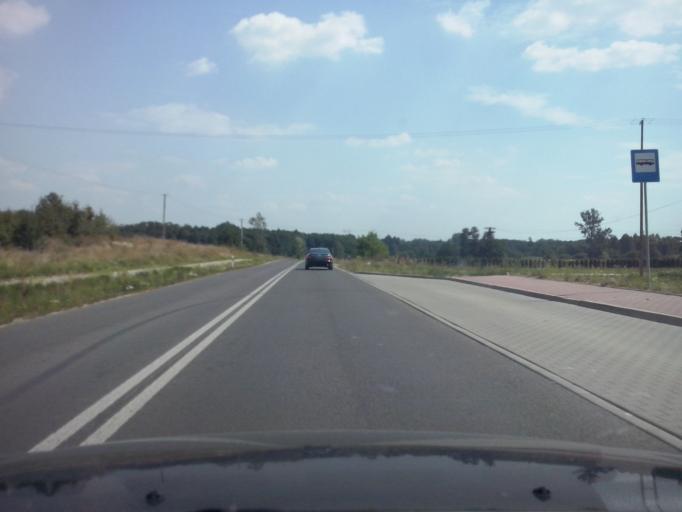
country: PL
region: Swietokrzyskie
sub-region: Powiat kielecki
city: Chmielnik
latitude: 50.6165
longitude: 20.7756
